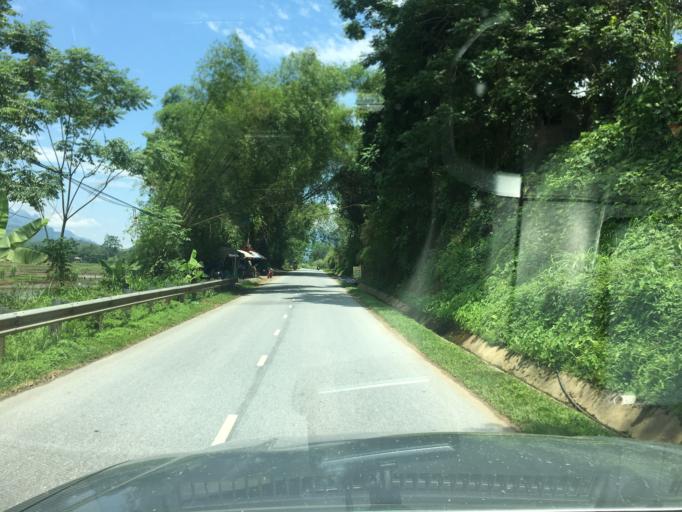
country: VN
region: Yen Bai
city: Son Thinh
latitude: 21.6302
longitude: 104.5055
